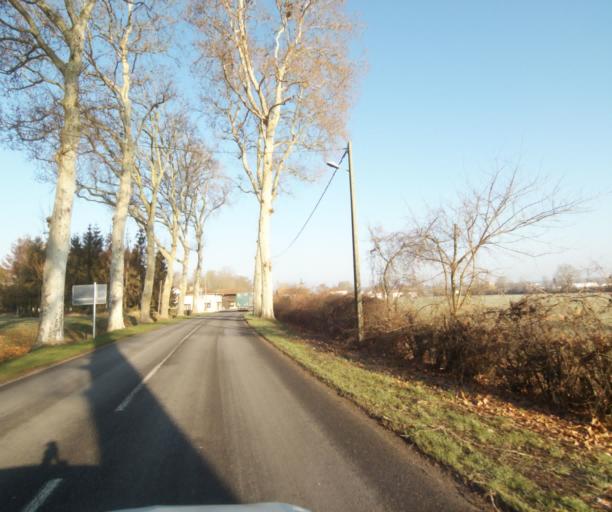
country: FR
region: Champagne-Ardenne
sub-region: Departement de la Haute-Marne
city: Montier-en-Der
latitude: 48.4665
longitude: 4.7636
